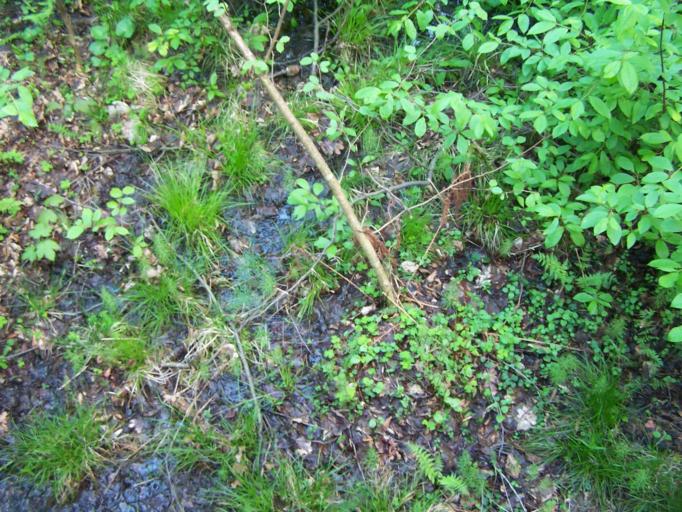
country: PL
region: Swietokrzyskie
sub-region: Powiat starachowicki
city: Brody
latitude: 51.0529
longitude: 21.1765
